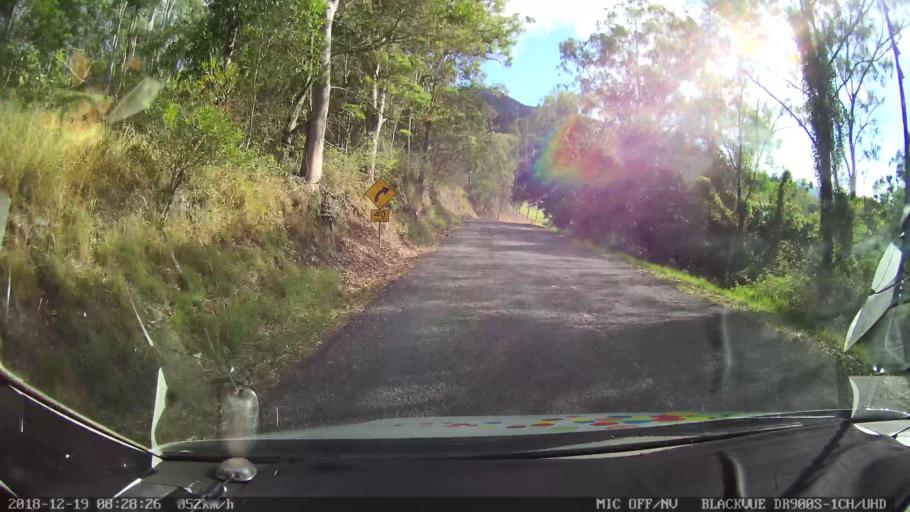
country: AU
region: New South Wales
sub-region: Kyogle
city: Kyogle
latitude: -28.3208
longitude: 152.9315
